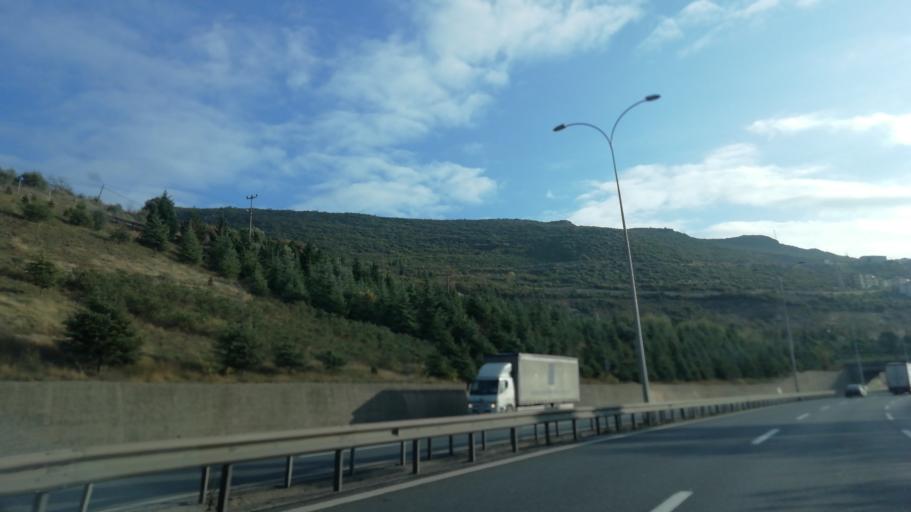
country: TR
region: Kocaeli
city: Hereke
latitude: 40.7885
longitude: 29.6172
